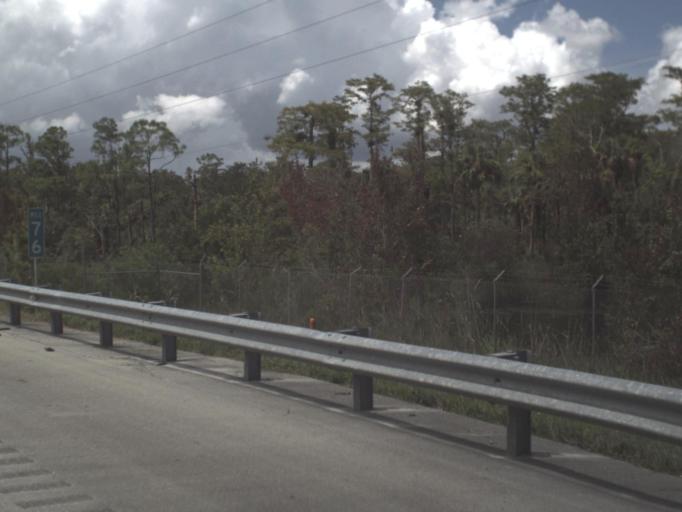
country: US
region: Florida
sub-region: Collier County
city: Immokalee
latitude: 26.1556
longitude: -81.2787
